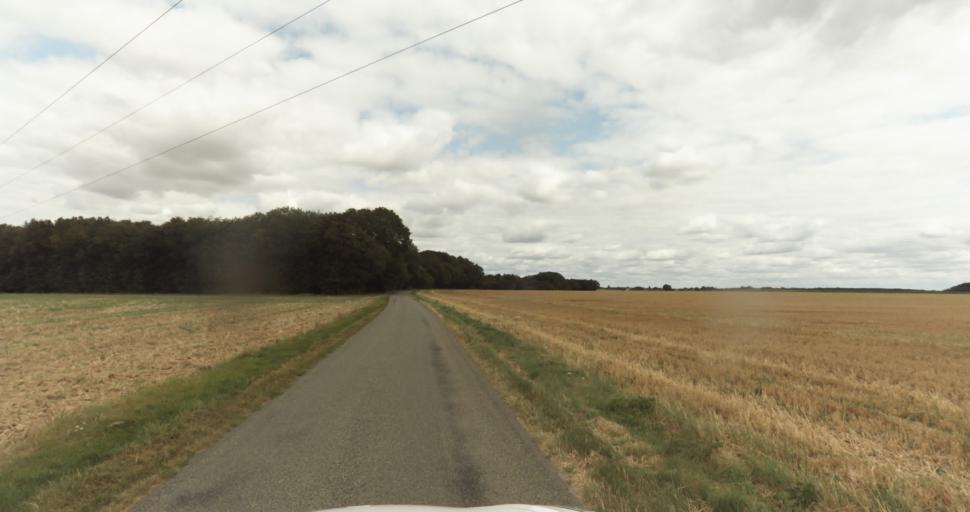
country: FR
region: Haute-Normandie
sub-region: Departement de l'Eure
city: Saint-Germain-sur-Avre
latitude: 48.8096
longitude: 1.2530
